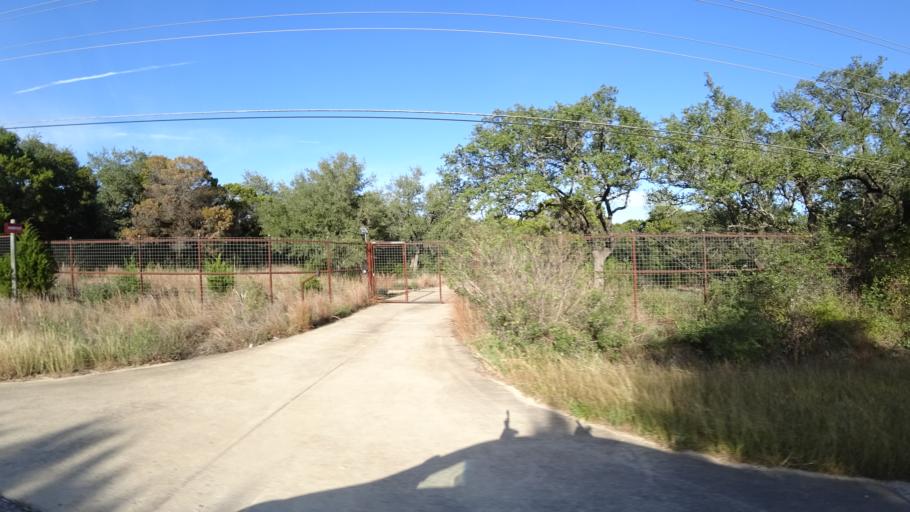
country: US
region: Texas
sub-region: Travis County
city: Barton Creek
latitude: 30.2422
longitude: -97.9222
